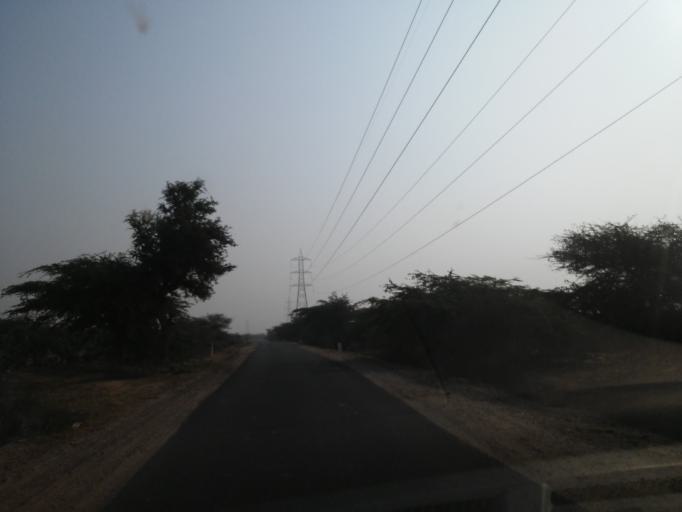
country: IN
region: Gujarat
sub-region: Kachchh
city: Mandvi
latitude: 22.8326
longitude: 69.5075
